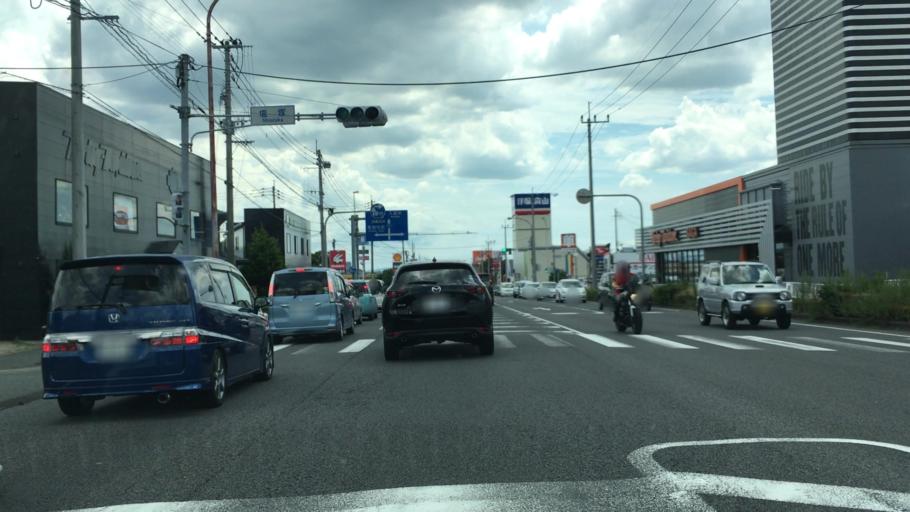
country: JP
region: Saga Prefecture
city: Tosu
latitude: 33.3810
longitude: 130.4991
